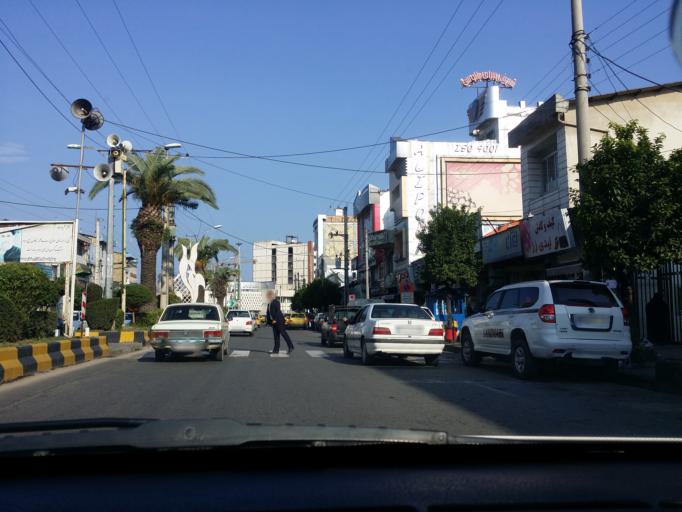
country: IR
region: Mazandaran
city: Chalus
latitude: 36.6534
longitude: 51.4216
